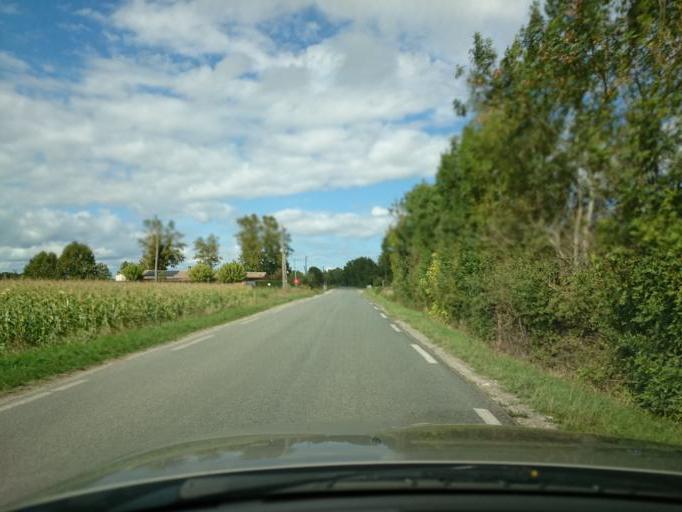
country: FR
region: Aquitaine
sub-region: Departement de la Gironde
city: Saint-Louis-de-Montferrand
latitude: 44.9655
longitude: -0.5530
